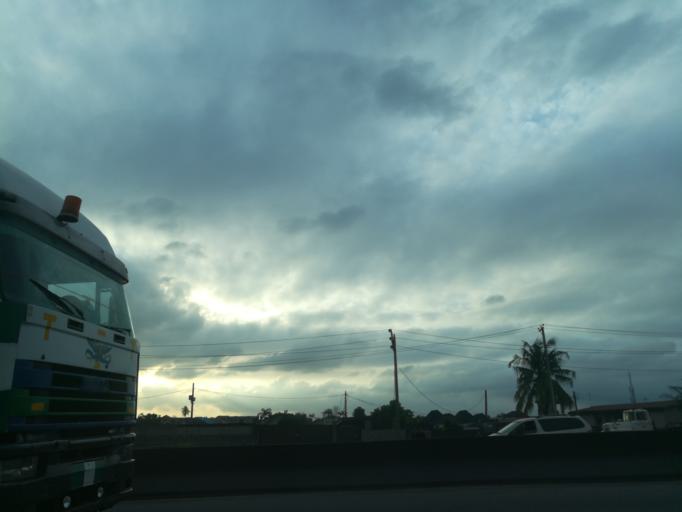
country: NG
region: Lagos
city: Ifako
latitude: 6.6329
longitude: 3.3659
